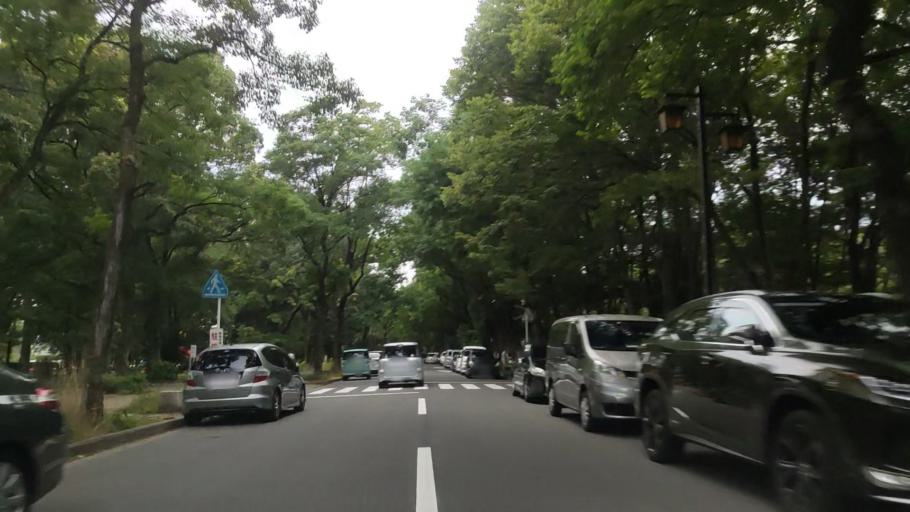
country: JP
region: Aichi
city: Nagoya-shi
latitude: 35.1869
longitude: 136.9025
